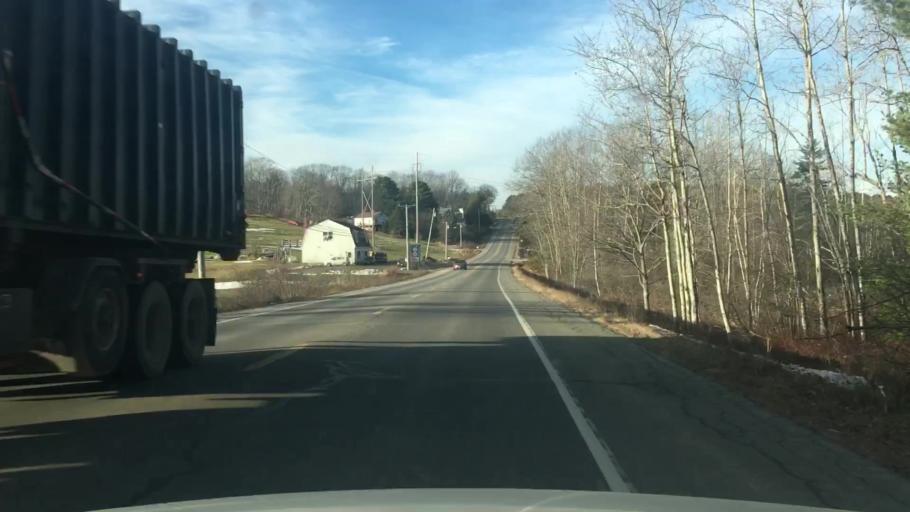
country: US
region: Maine
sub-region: Lincoln County
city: Wiscasset
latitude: 44.0415
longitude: -69.6752
